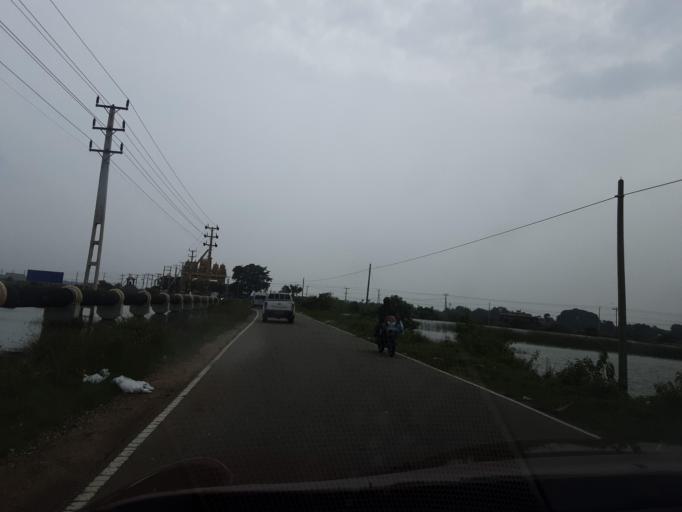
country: LK
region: Northern Province
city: Jaffna
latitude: 9.6639
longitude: 80.0601
